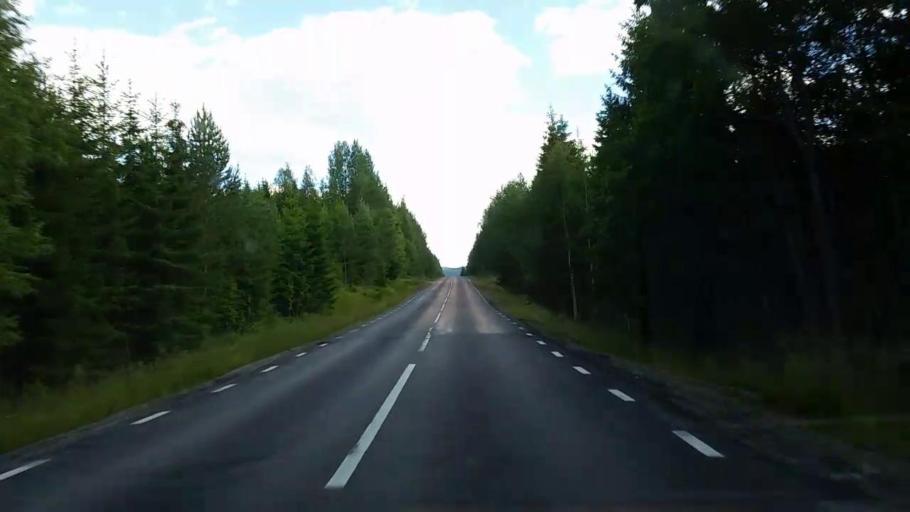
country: SE
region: Gaevleborg
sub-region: Ljusdals Kommun
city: Farila
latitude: 62.1449
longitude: 15.6856
